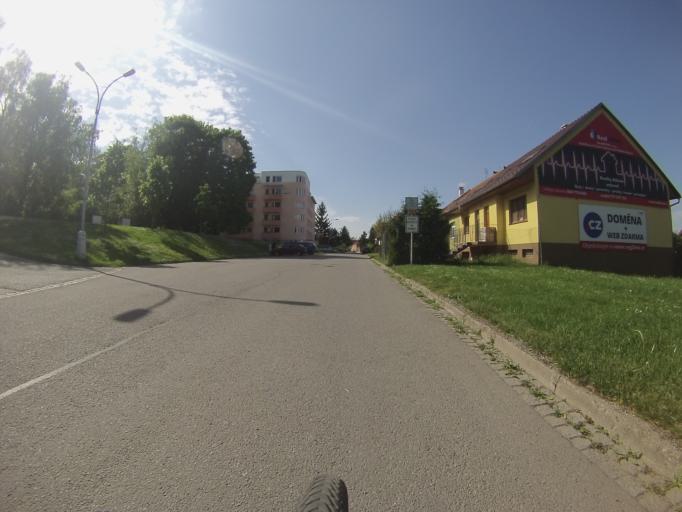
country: CZ
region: South Moravian
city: Troubsko
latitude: 49.2241
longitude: 16.5305
